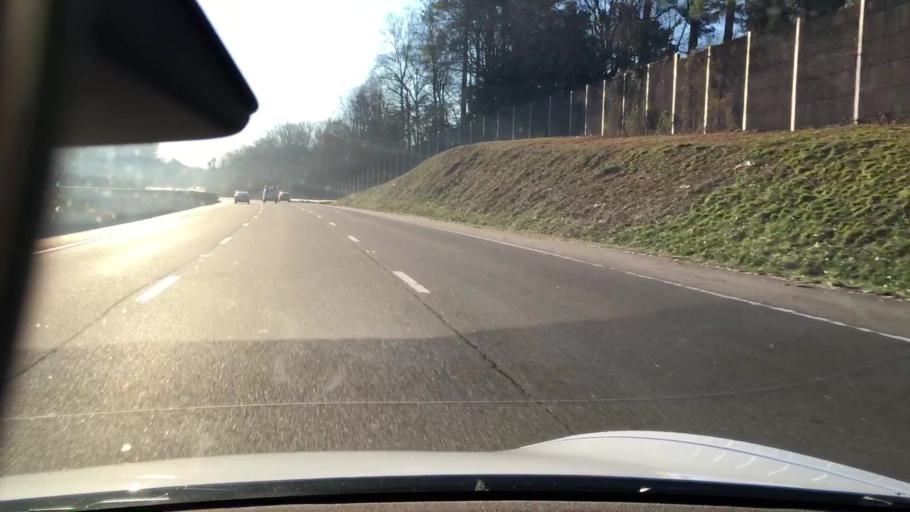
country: US
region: Virginia
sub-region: Chesterfield County
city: Bensley
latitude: 37.4671
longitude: -77.5066
